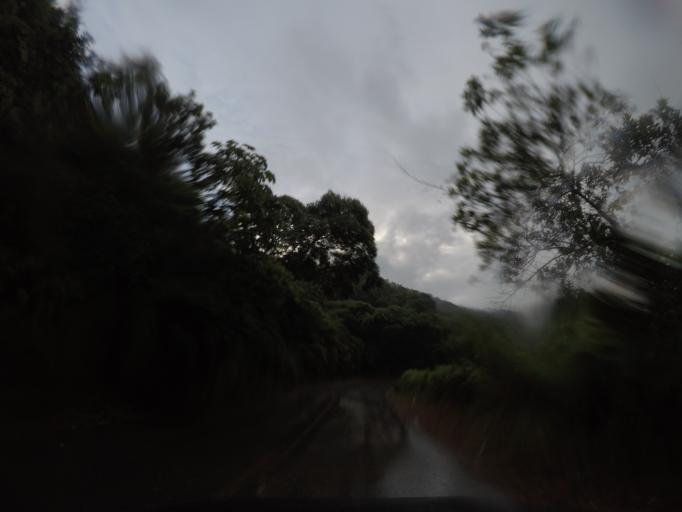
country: MX
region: Oaxaca
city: San Gabriel Mixtepec
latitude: 16.0710
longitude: -97.0780
